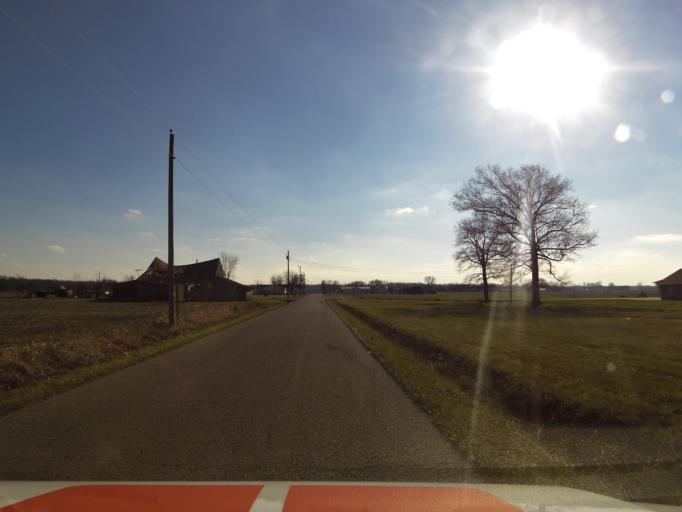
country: US
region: Indiana
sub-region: Jackson County
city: Seymour
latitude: 38.9850
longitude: -85.7975
